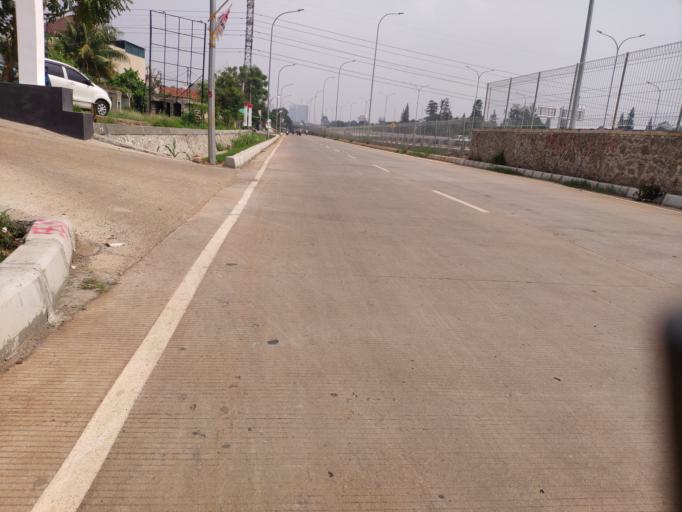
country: ID
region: West Java
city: Pamulang
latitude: -6.3194
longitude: 106.8033
